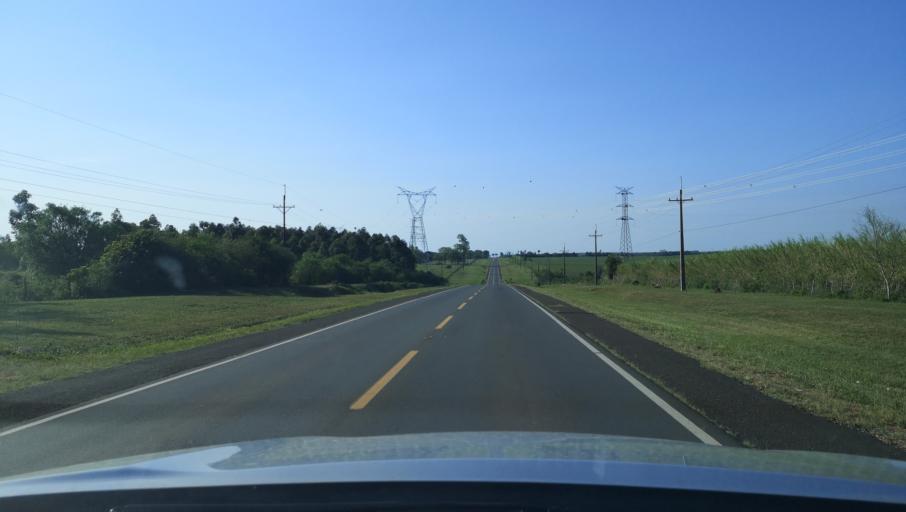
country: PY
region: Misiones
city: Santa Maria
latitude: -26.7922
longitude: -57.0242
